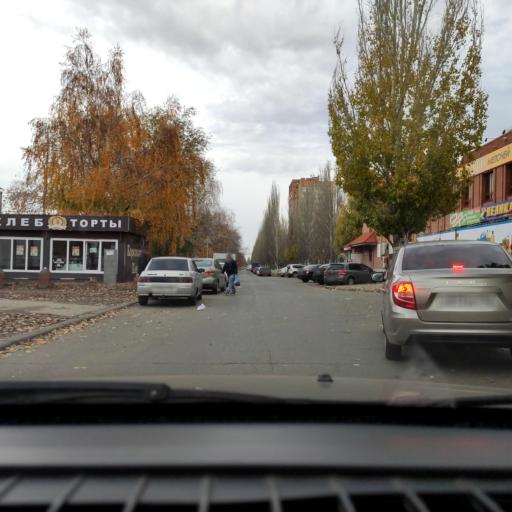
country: RU
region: Samara
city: Tol'yatti
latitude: 53.5301
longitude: 49.2983
